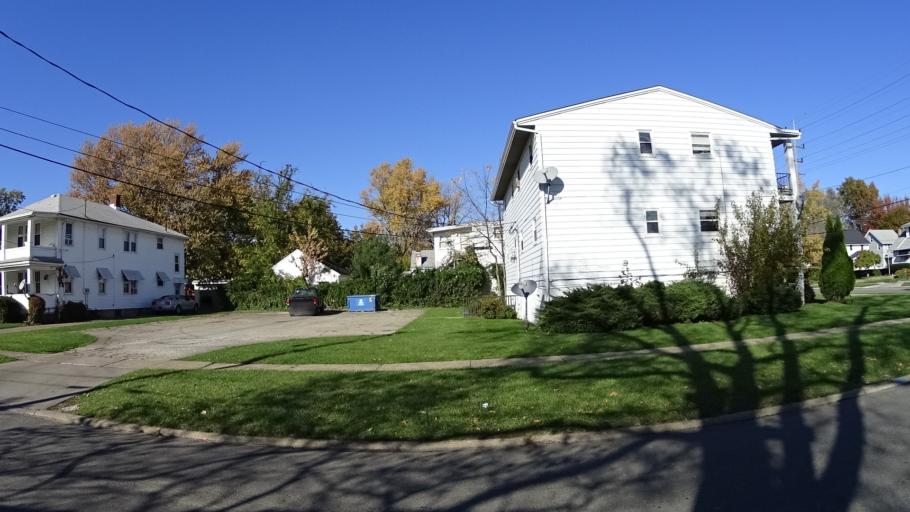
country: US
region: Ohio
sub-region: Lorain County
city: Lorain
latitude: 41.4583
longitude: -82.1855
